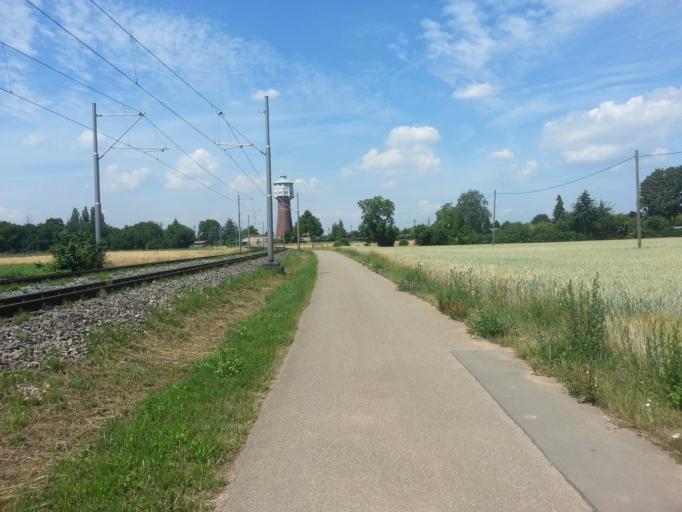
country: DE
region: Baden-Wuerttemberg
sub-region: Karlsruhe Region
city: Edingen-Neckarhausen
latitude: 49.4366
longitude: 8.6296
